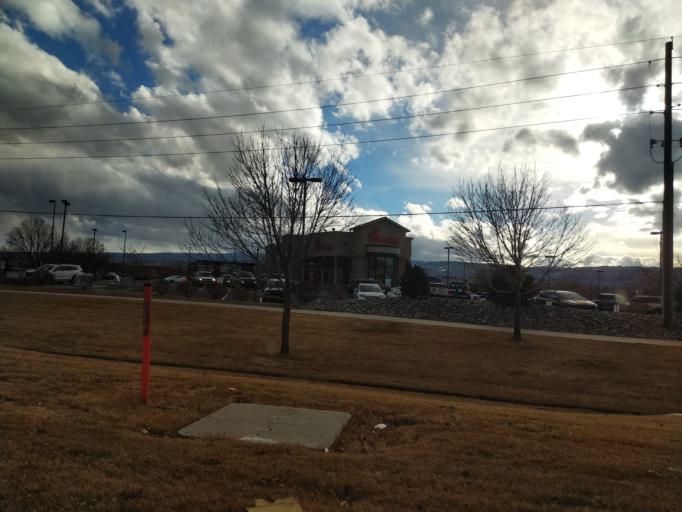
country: US
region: Colorado
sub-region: Mesa County
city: Grand Junction
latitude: 39.0807
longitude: -108.5841
